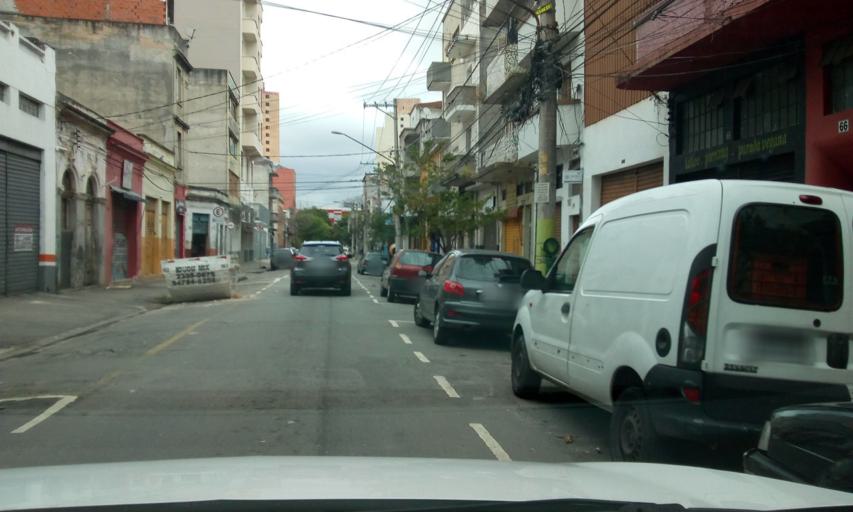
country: BR
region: Sao Paulo
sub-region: Sao Paulo
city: Sao Paulo
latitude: -23.5472
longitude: -46.6230
